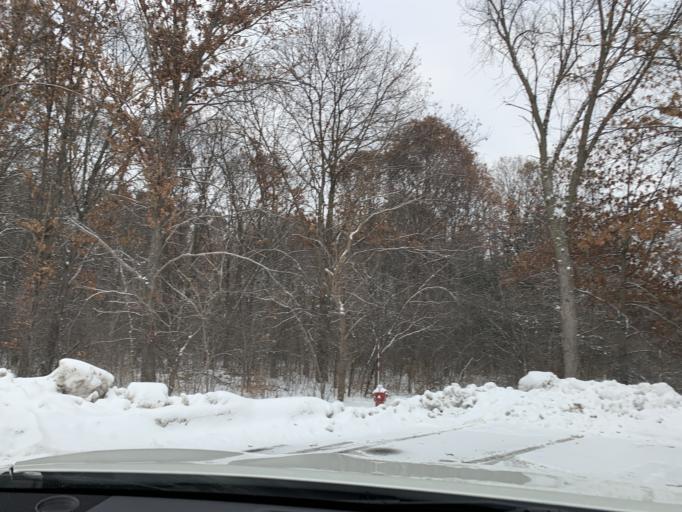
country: US
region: Minnesota
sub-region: Anoka County
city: Coon Rapids
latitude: 45.1549
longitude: -93.3047
